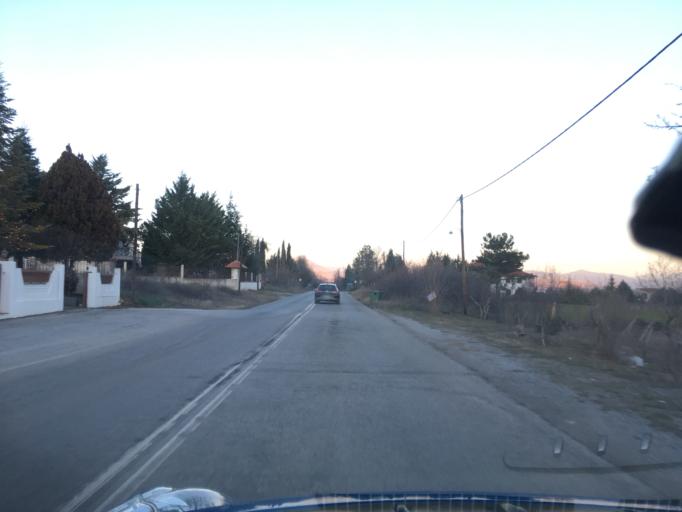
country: GR
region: West Macedonia
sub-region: Nomos Kozanis
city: Kozani
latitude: 40.2659
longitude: 21.7687
